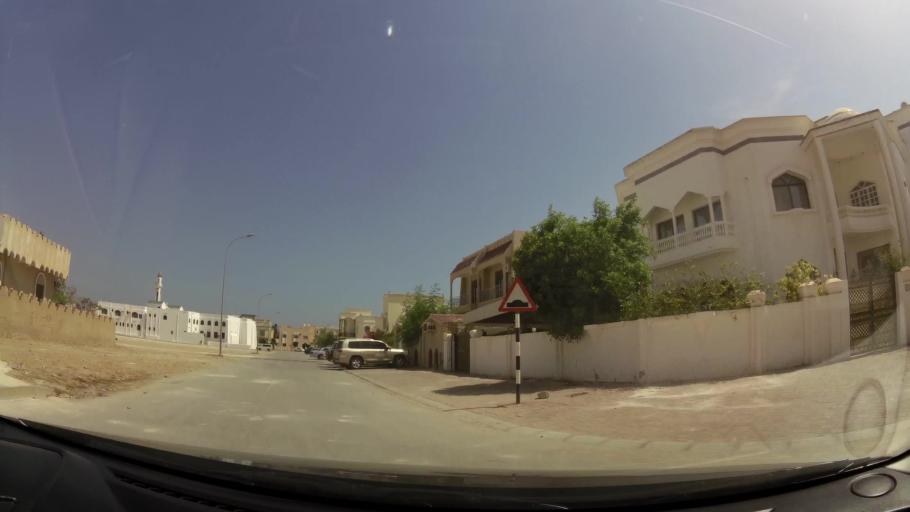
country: OM
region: Zufar
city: Salalah
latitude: 17.0415
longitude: 54.1521
